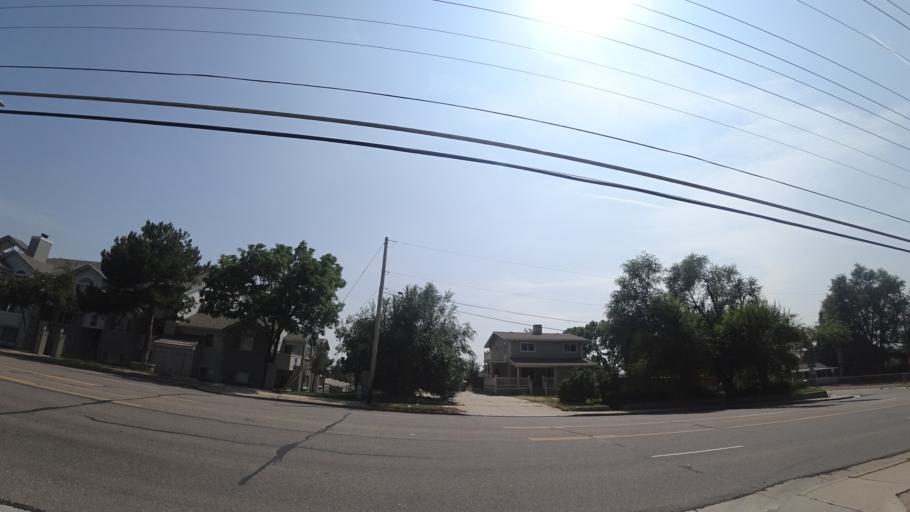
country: US
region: Colorado
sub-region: Arapahoe County
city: Englewood
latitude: 39.6242
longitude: -104.9938
